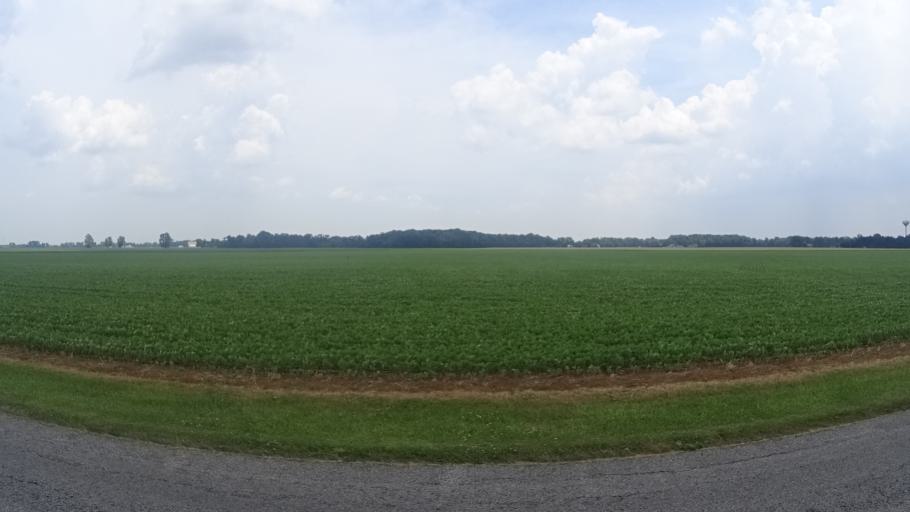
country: US
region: Ohio
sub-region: Erie County
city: Milan
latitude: 41.3012
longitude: -82.6535
